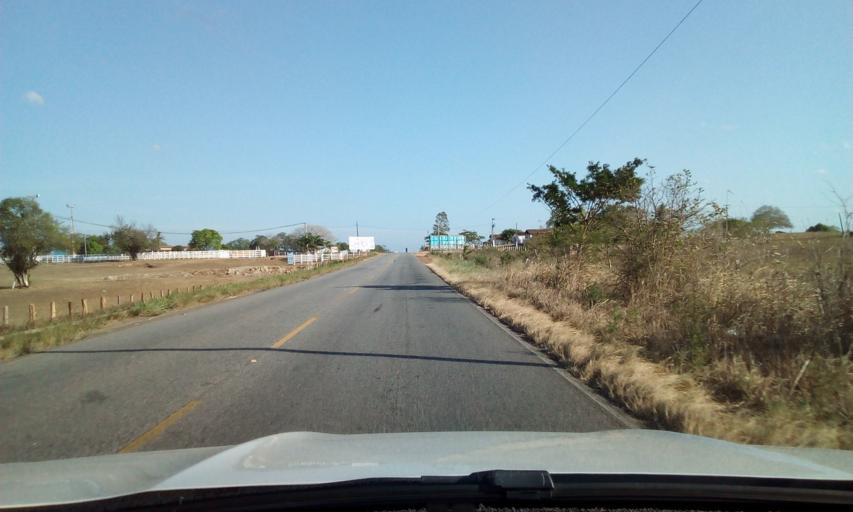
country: BR
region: Paraiba
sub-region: Guarabira
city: Guarabira
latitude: -6.9262
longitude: -35.4420
